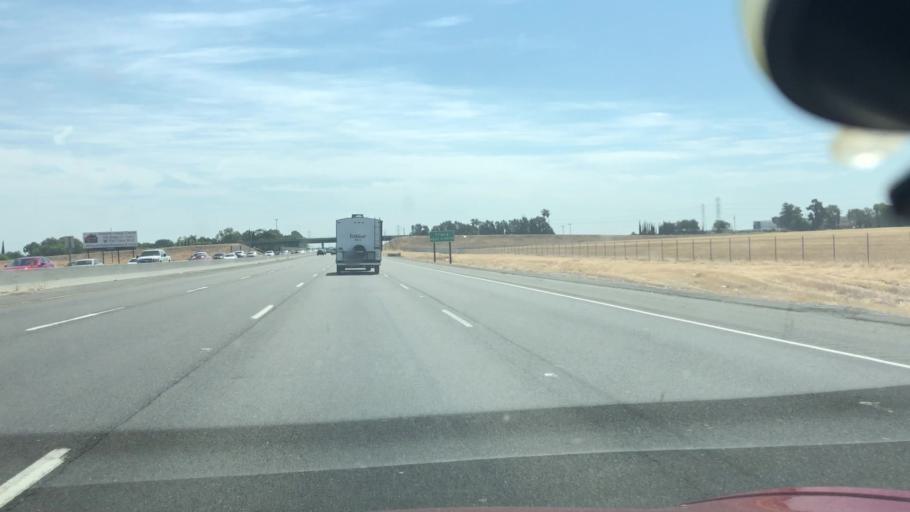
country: US
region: California
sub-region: San Joaquin County
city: Mountain House
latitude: 37.7415
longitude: -121.5180
